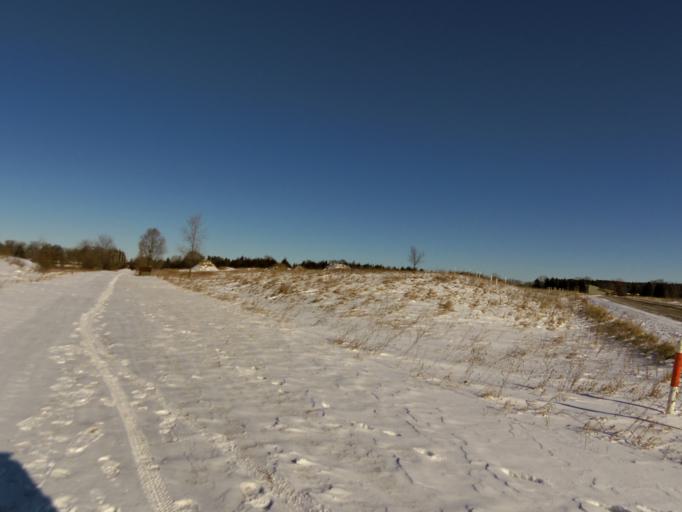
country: US
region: Minnesota
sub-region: Washington County
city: Lake Elmo
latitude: 44.9927
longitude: -92.8983
